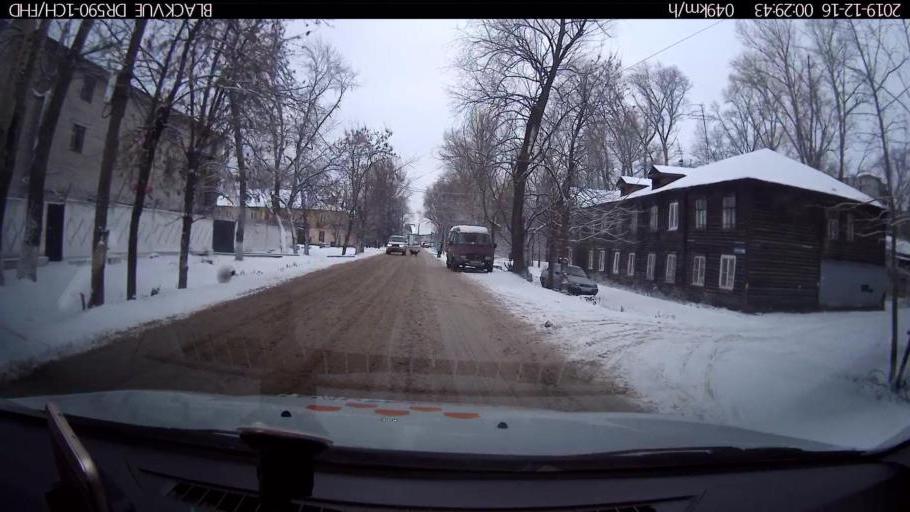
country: RU
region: Nizjnij Novgorod
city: Nizhniy Novgorod
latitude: 56.3104
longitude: 43.8905
